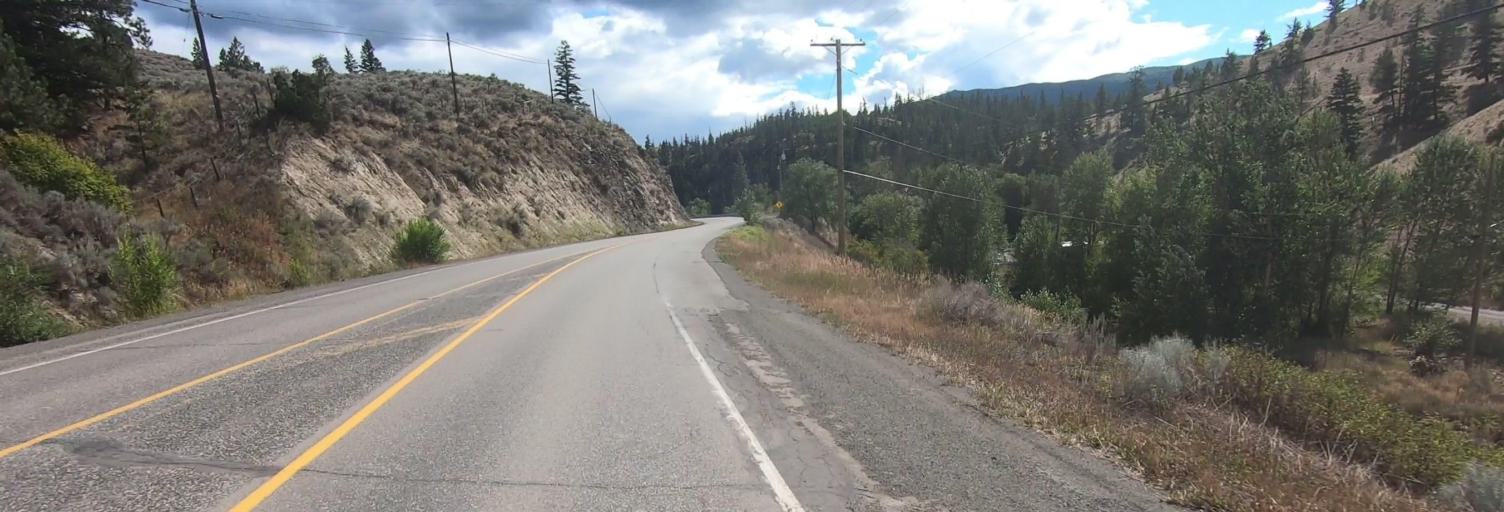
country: CA
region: British Columbia
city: Kamloops
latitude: 50.6790
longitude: -120.5757
